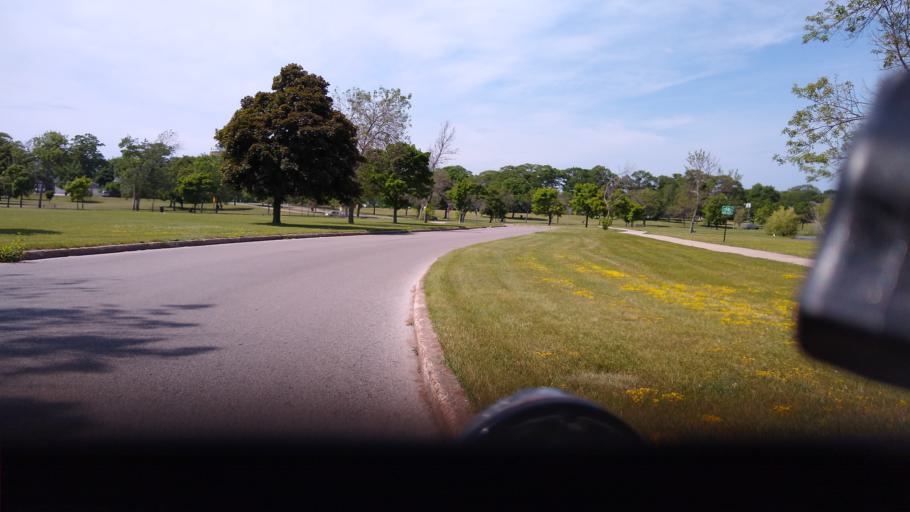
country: US
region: Michigan
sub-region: Delta County
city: Escanaba
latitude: 45.7403
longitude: -87.0495
